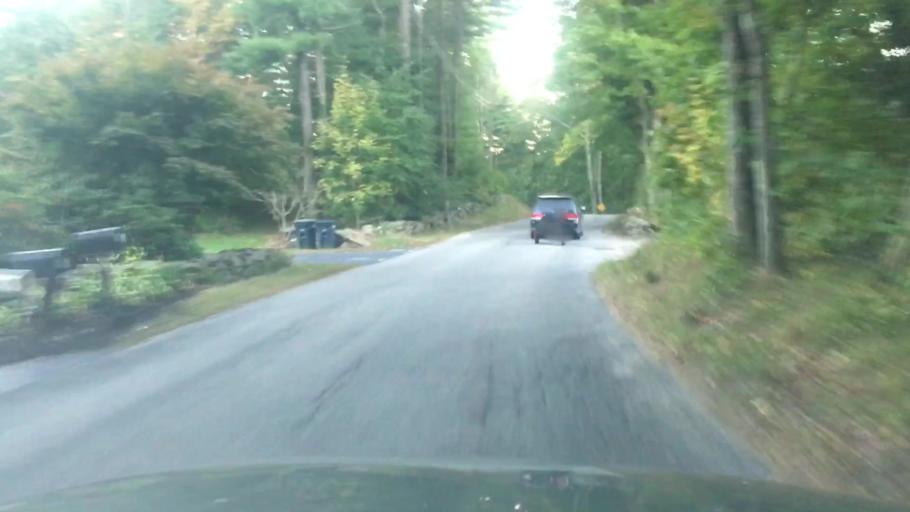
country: US
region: Massachusetts
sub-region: Worcester County
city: Southbridge
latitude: 42.1216
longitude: -72.0293
